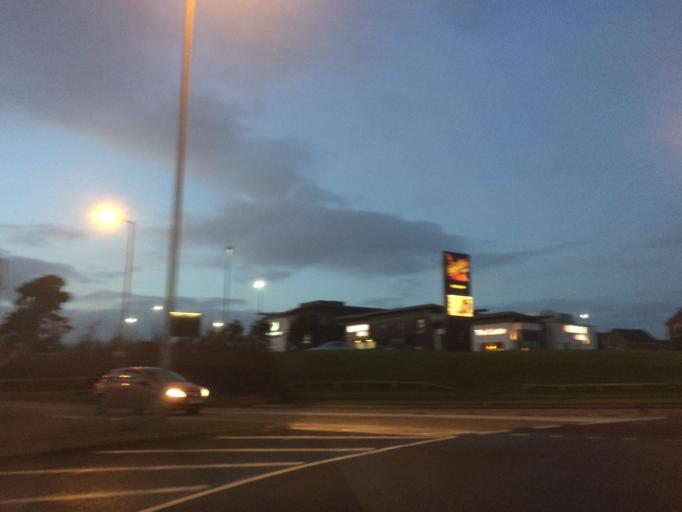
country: GB
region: Scotland
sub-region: East Renfrewshire
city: Newton Mearns
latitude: 55.7837
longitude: -4.3472
